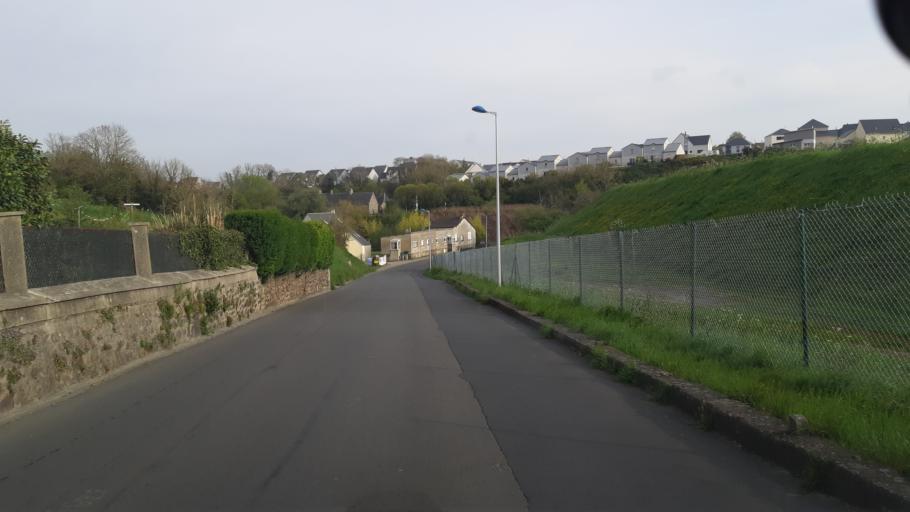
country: FR
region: Lower Normandy
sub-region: Departement de la Manche
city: Donville-les-Bains
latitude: 48.8451
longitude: -1.5769
